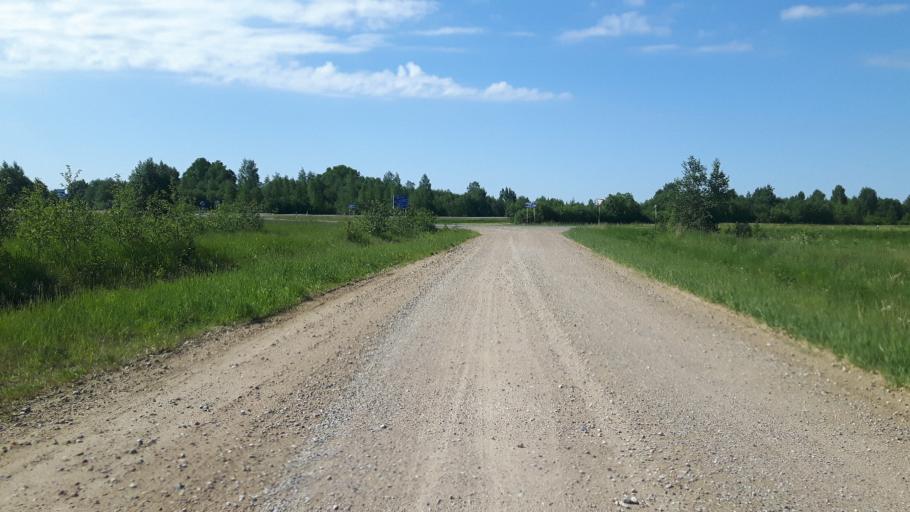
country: EE
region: Paernumaa
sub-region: Vaendra vald (alev)
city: Vandra
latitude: 58.6637
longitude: 25.0243
